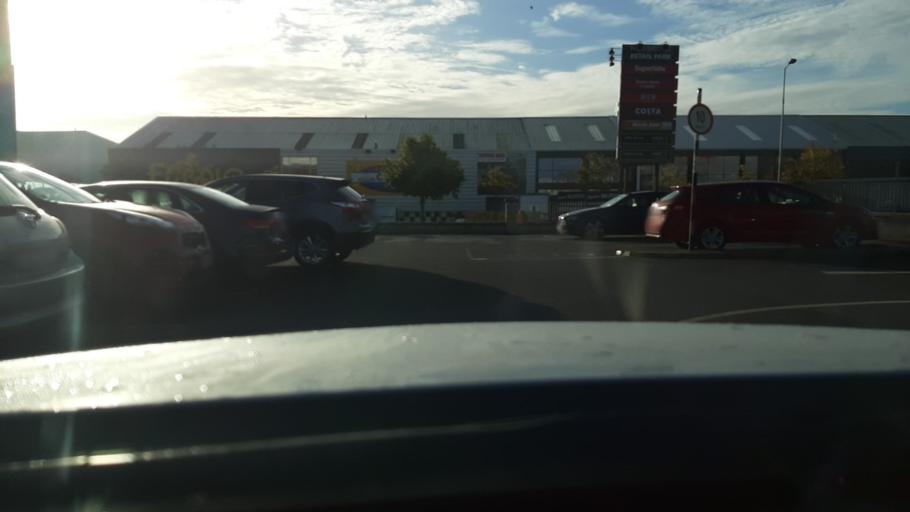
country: IE
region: Leinster
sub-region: Kildare
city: Droichead Nua
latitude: 53.1753
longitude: -6.8006
